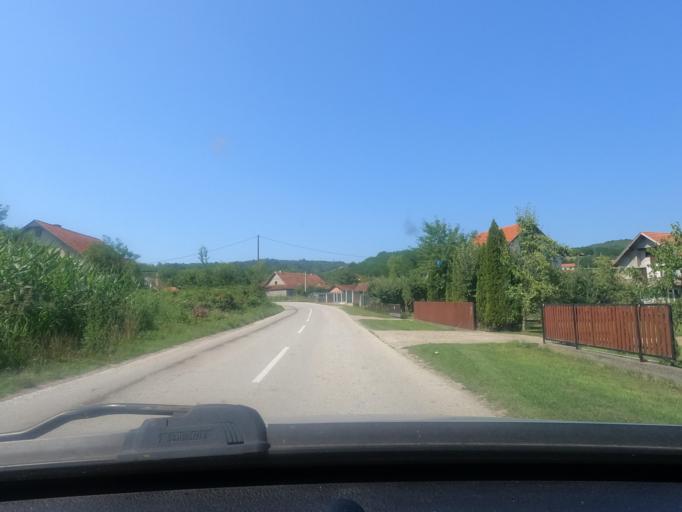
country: RS
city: Jadranska Lesnica
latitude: 44.5462
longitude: 19.3542
